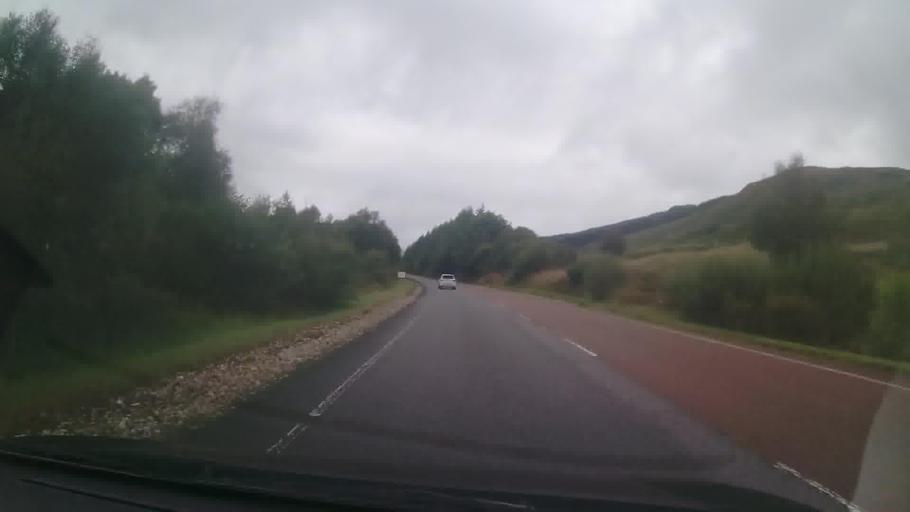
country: GB
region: Scotland
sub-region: Argyll and Bute
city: Garelochhead
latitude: 56.4238
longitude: -4.6788
